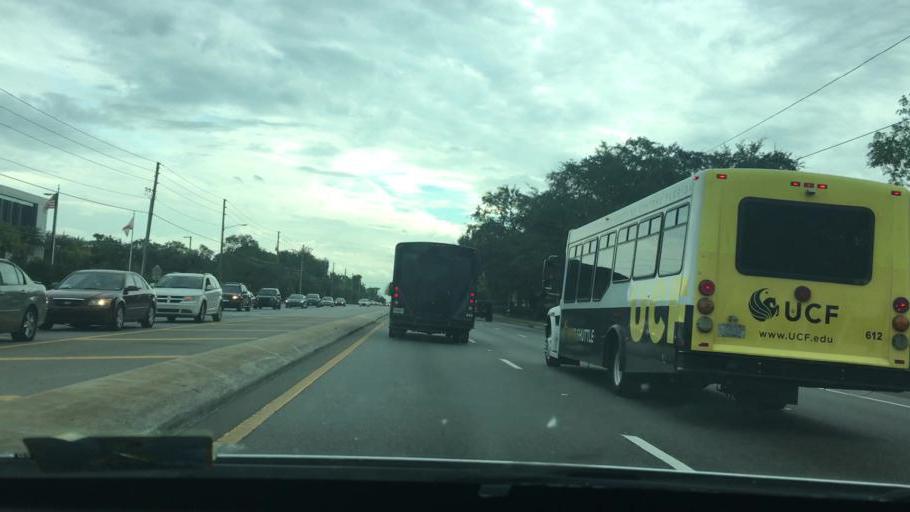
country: US
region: Florida
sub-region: Orange County
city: Alafaya
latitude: 28.5828
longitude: -81.2078
